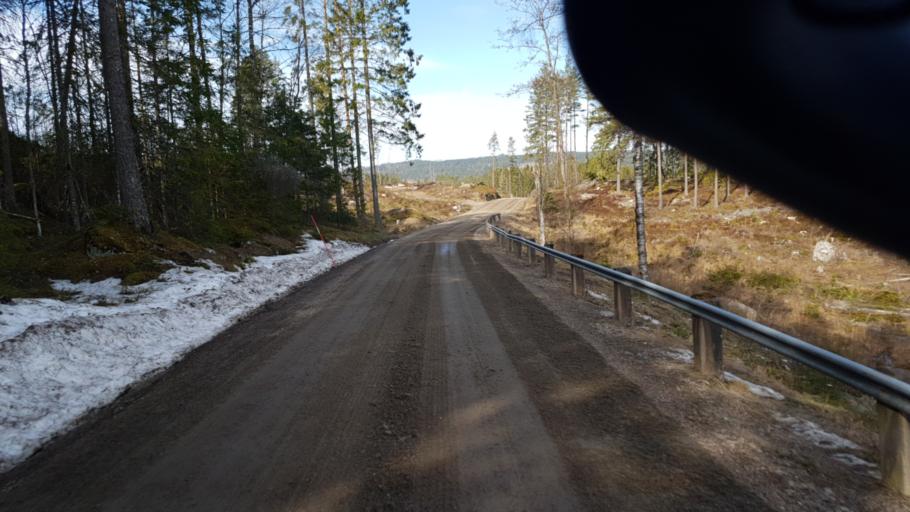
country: SE
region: Vaermland
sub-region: Arvika Kommun
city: Arvika
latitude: 59.5413
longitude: 12.4413
